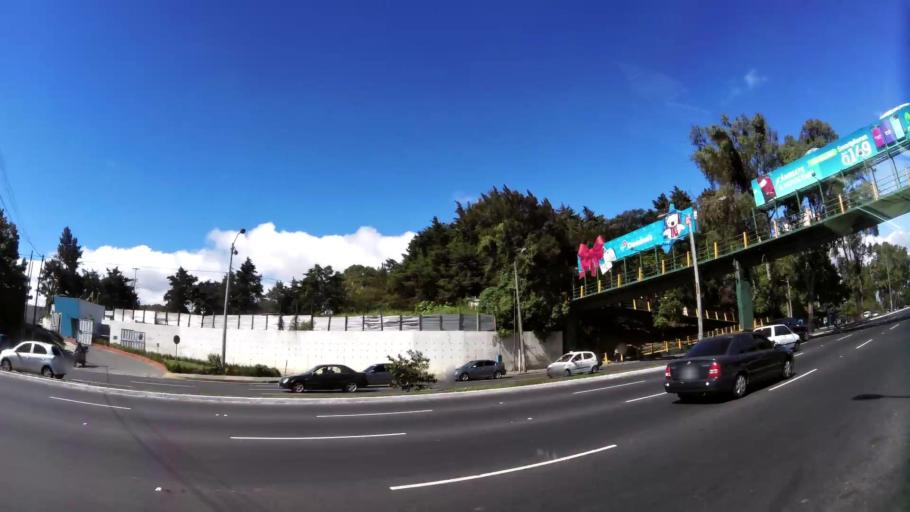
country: GT
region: Guatemala
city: Guatemala City
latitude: 14.6079
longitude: -90.5315
